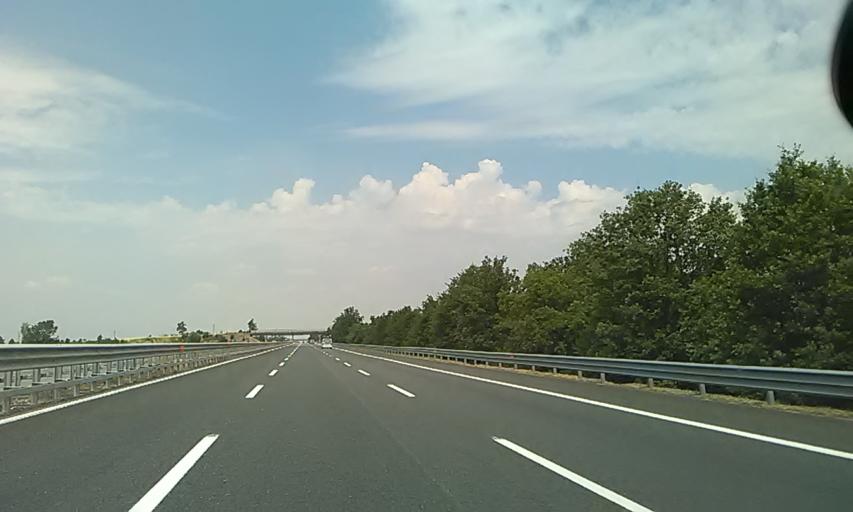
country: IT
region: Piedmont
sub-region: Provincia di Alessandria
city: Predosa
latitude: 44.7776
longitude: 8.6250
